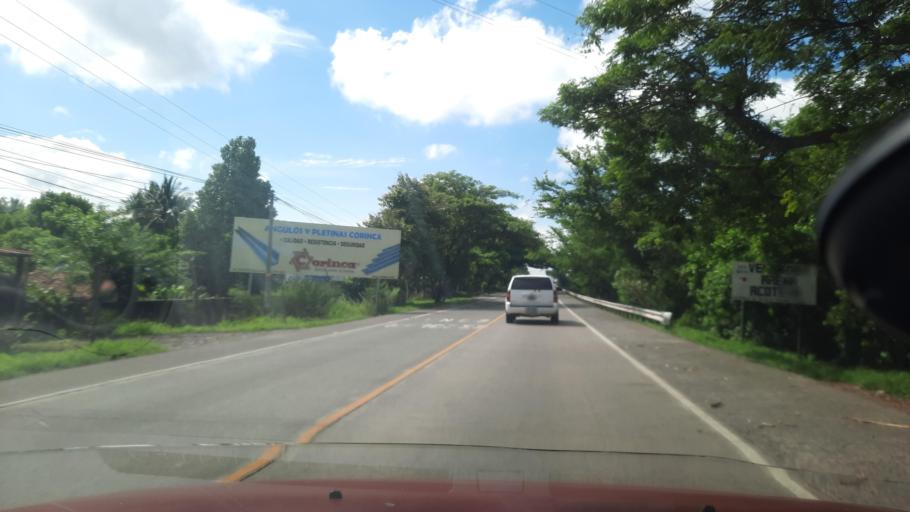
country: SV
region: Usulutan
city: San Agustin
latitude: 13.4279
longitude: -88.7037
